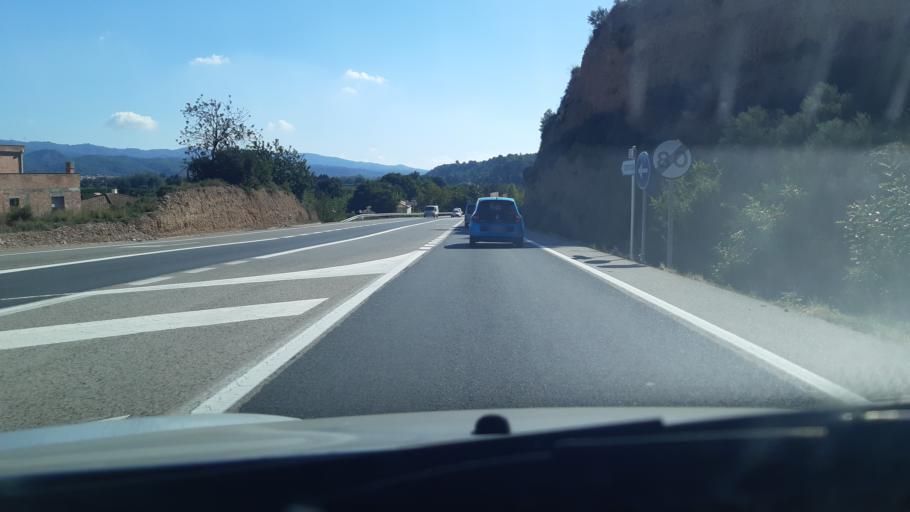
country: ES
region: Catalonia
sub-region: Provincia de Tarragona
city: Tivenys
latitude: 40.8770
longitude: 0.5002
